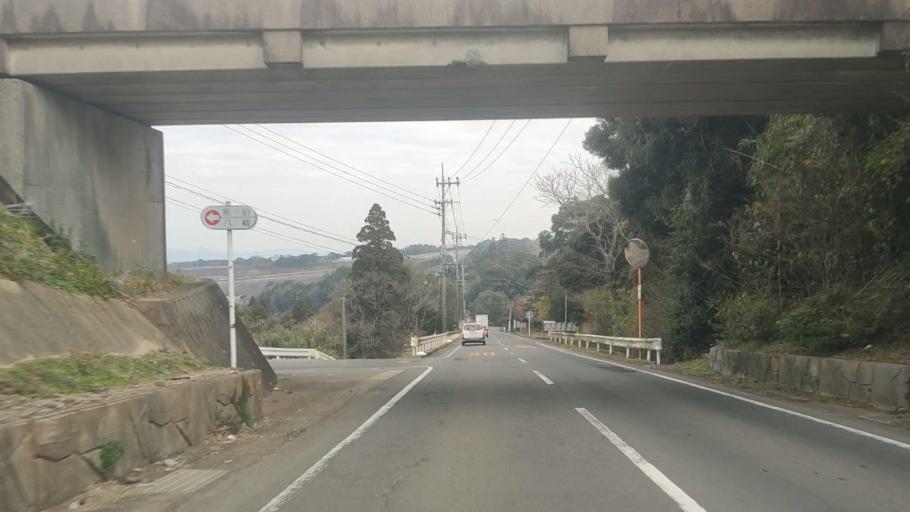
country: JP
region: Nagasaki
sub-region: Isahaya-shi
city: Isahaya
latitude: 32.8099
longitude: 130.1707
